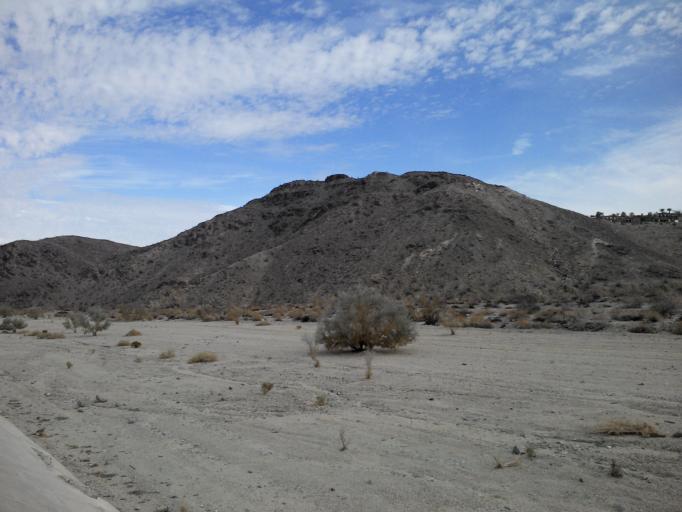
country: US
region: California
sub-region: Riverside County
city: Cathedral City
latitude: 33.7708
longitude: -116.4651
